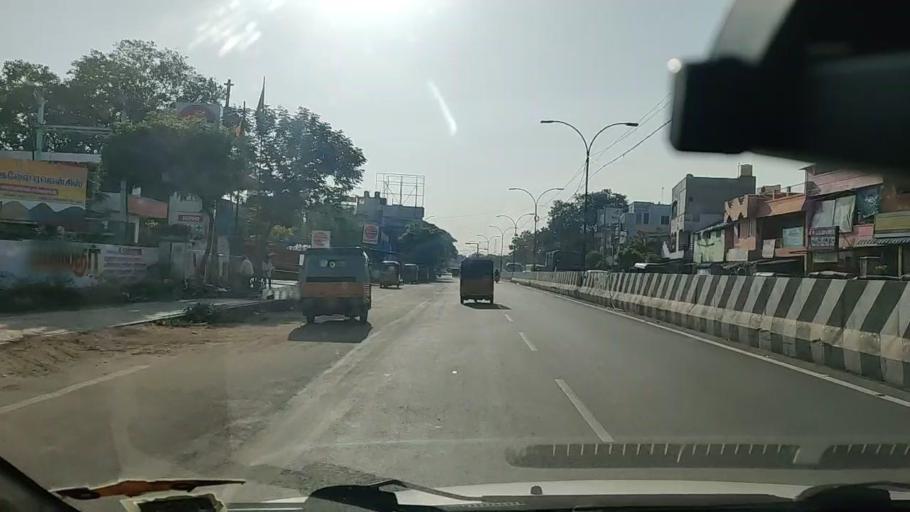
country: IN
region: Tamil Nadu
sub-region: Chennai
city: George Town
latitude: 13.1188
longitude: 80.2574
